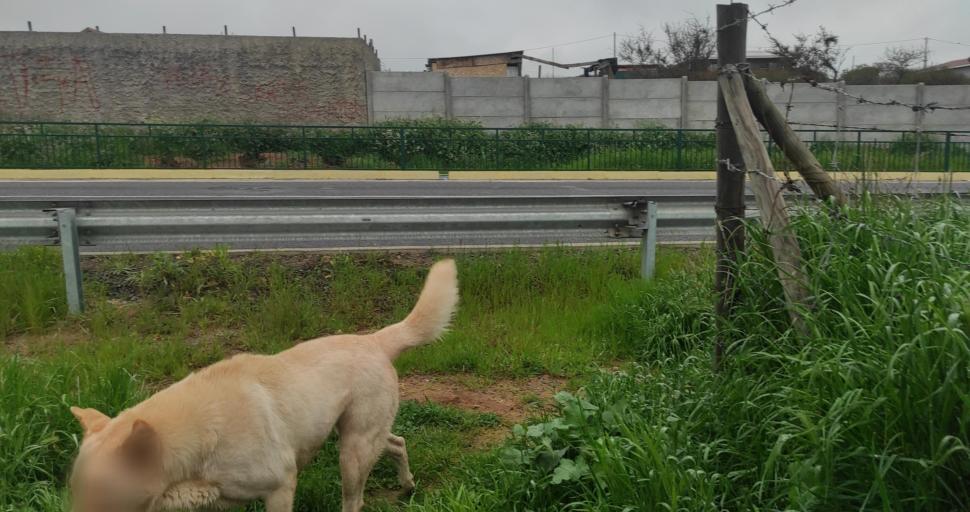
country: CL
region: Valparaiso
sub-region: Provincia de Marga Marga
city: Limache
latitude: -33.0222
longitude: -71.2609
